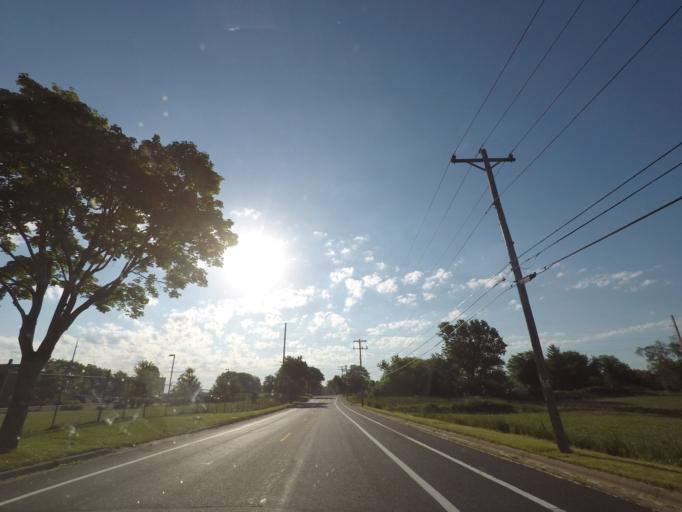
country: US
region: Wisconsin
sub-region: Dane County
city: Monona
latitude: 43.0328
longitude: -89.3611
